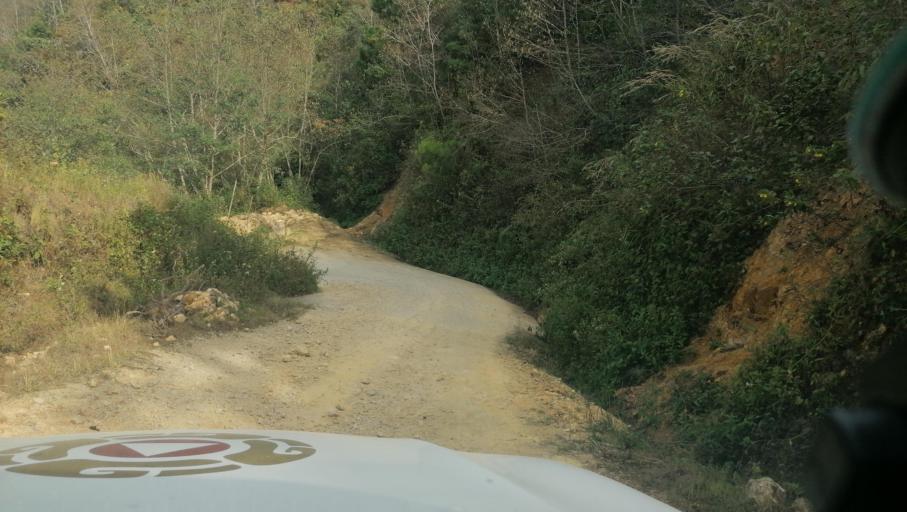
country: GT
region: San Marcos
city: Tacana
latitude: 15.2196
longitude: -92.1964
